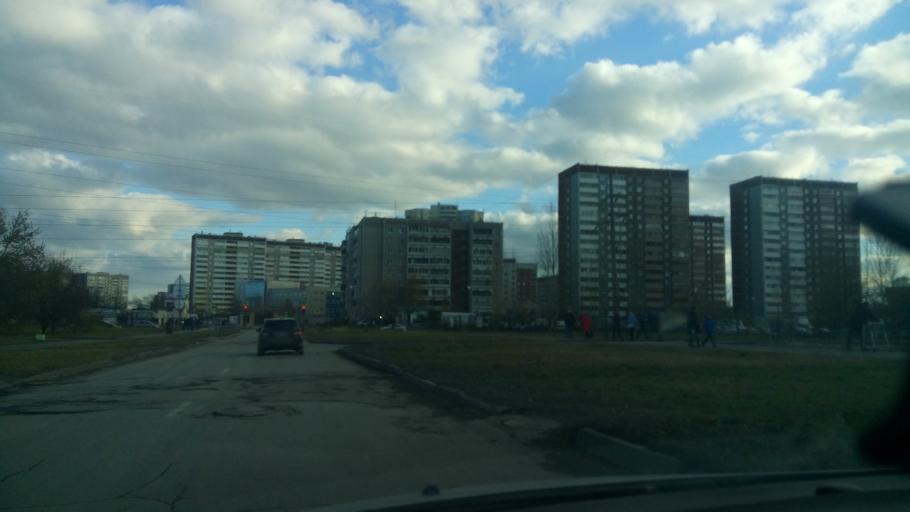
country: RU
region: Sverdlovsk
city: Yekaterinburg
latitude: 56.8658
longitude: 60.5412
